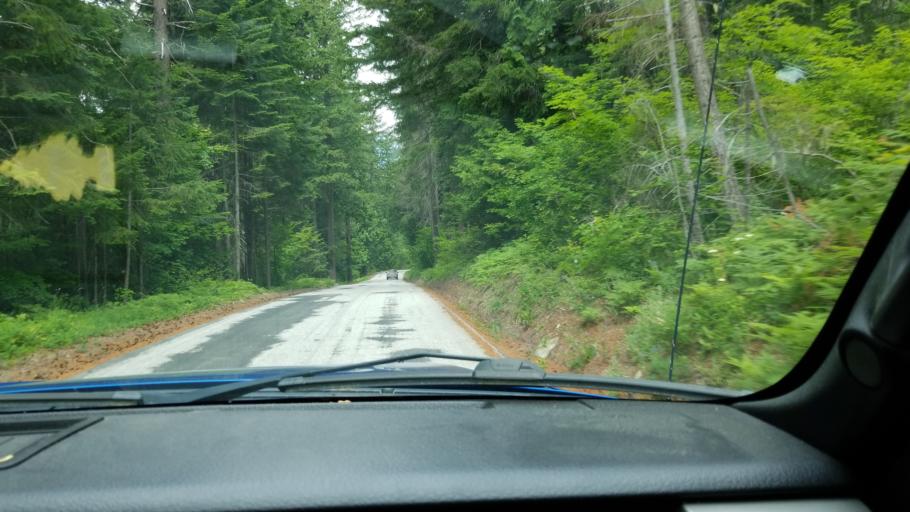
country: US
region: Washington
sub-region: Chelan County
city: Leavenworth
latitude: 47.8588
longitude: -120.8458
